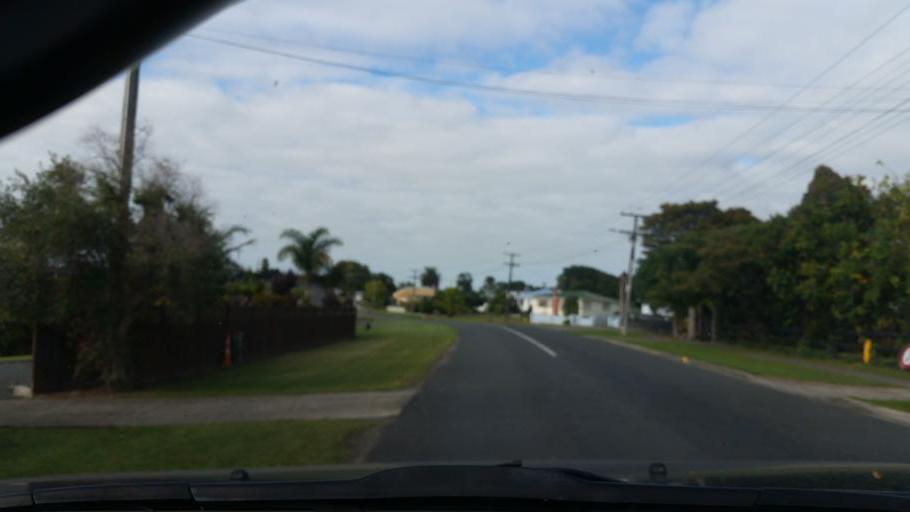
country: NZ
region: Northland
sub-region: Kaipara District
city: Dargaville
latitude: -35.9275
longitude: 173.8692
